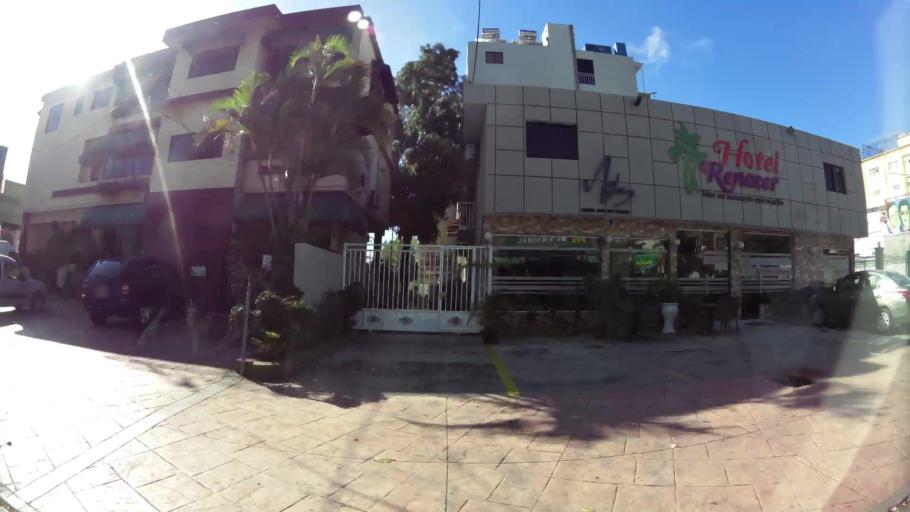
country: DO
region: Nacional
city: Ciudad Nueva
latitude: 18.4707
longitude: -69.8966
